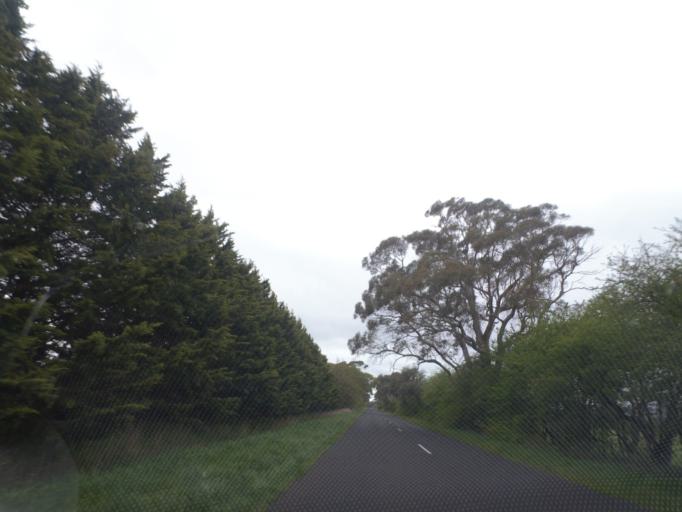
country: AU
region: Victoria
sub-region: Hume
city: Sunbury
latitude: -37.3248
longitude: 144.5706
